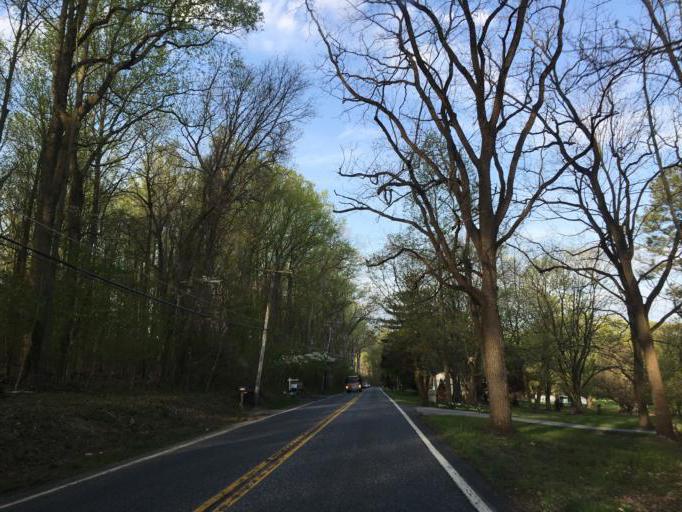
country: US
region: Maryland
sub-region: Baltimore County
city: Reisterstown
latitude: 39.4820
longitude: -76.7923
